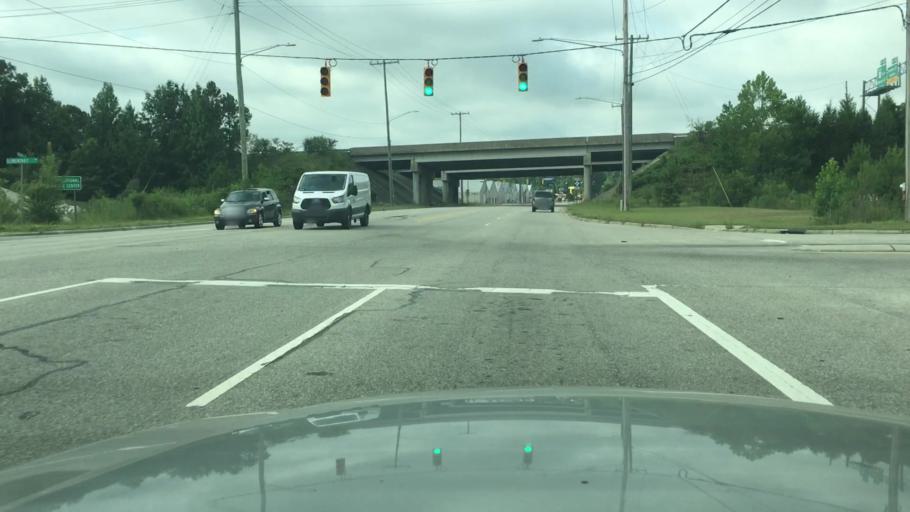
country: US
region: North Carolina
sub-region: Cumberland County
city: Fayetteville
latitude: 35.0387
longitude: -78.8832
